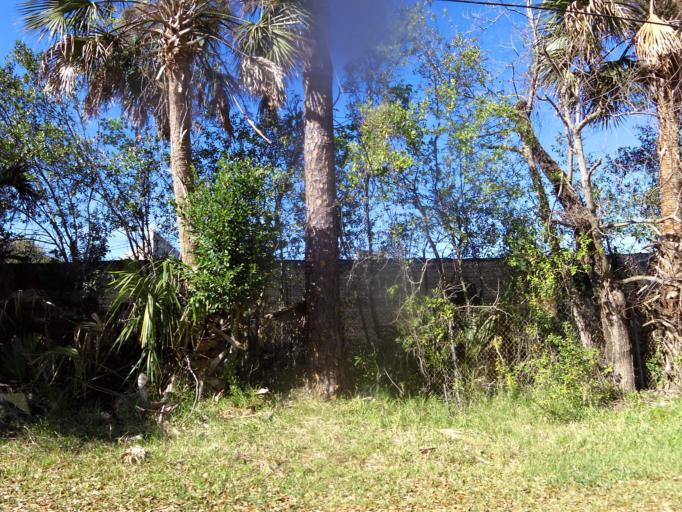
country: US
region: Florida
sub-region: Duval County
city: Jacksonville
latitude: 30.3741
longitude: -81.6498
